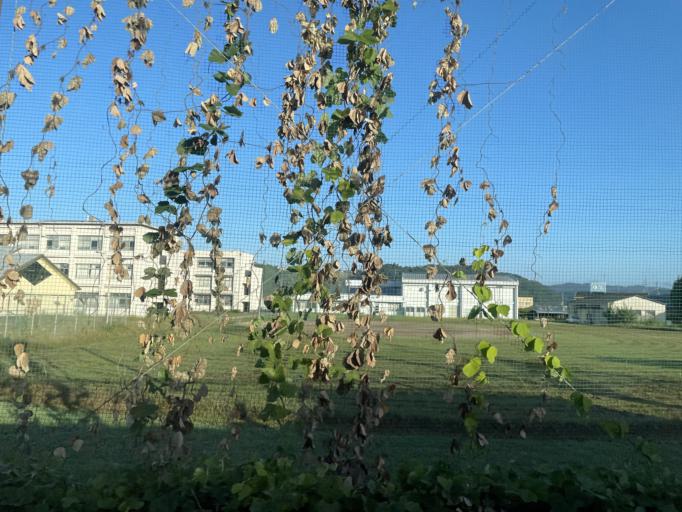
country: JP
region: Mie
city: Nabari
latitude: 34.6289
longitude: 136.1000
